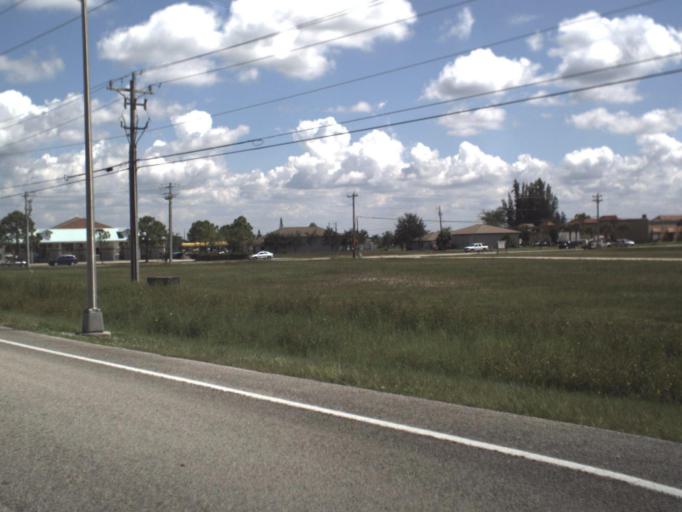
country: US
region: Florida
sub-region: Lee County
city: Lochmoor Waterway Estates
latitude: 26.6461
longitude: -81.9879
